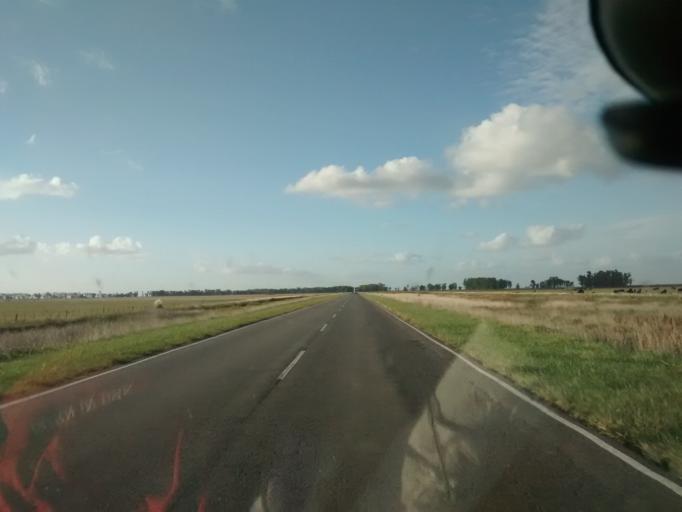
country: AR
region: Buenos Aires
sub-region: Partido de General Belgrano
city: General Belgrano
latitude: -36.1711
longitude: -58.5941
